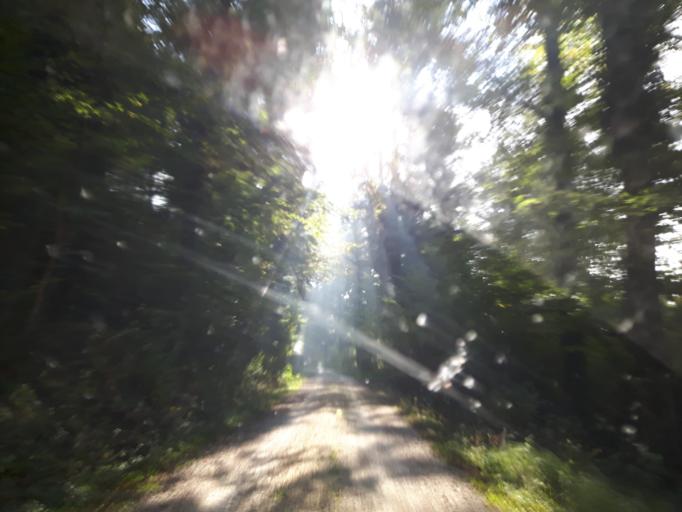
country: CH
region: Bern
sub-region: Oberaargau
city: Roggwil
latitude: 47.2407
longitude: 7.8351
